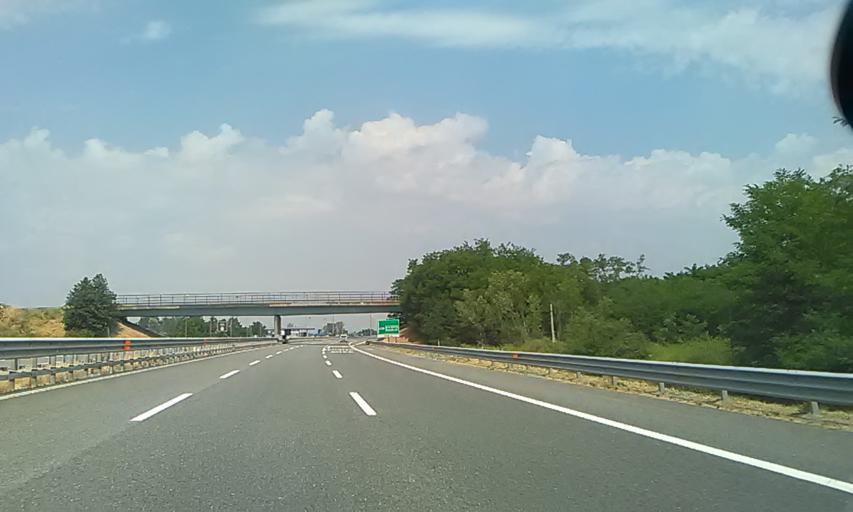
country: IT
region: Piedmont
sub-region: Provincia di Alessandria
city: Castelspina
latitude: 44.8134
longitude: 8.5962
